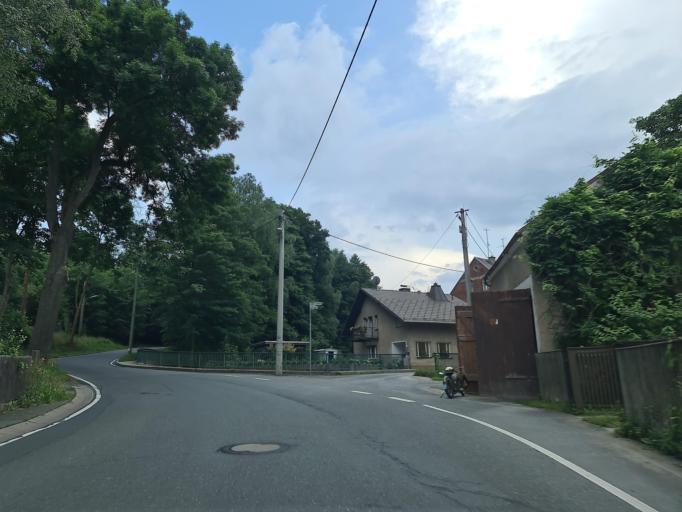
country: DE
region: Saxony
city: Bergen
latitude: 50.4697
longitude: 12.2744
